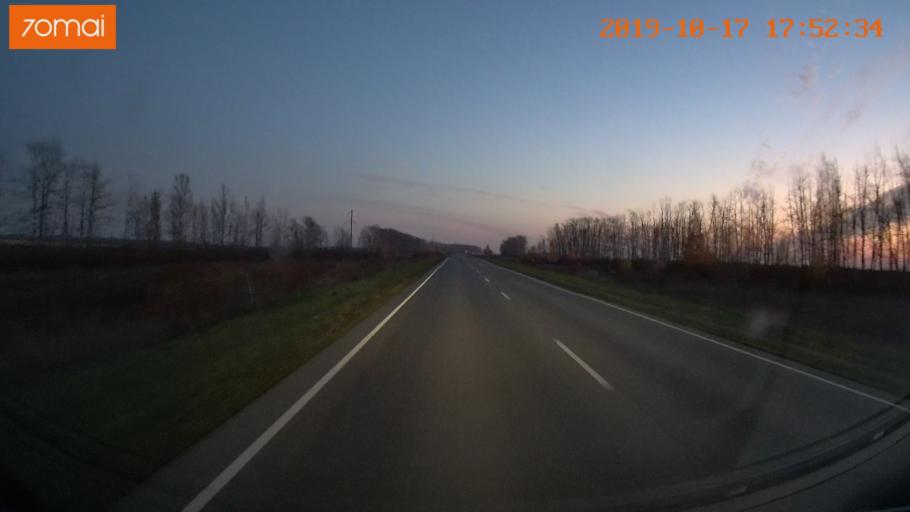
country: RU
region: Tula
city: Kurkino
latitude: 53.6329
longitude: 38.6831
